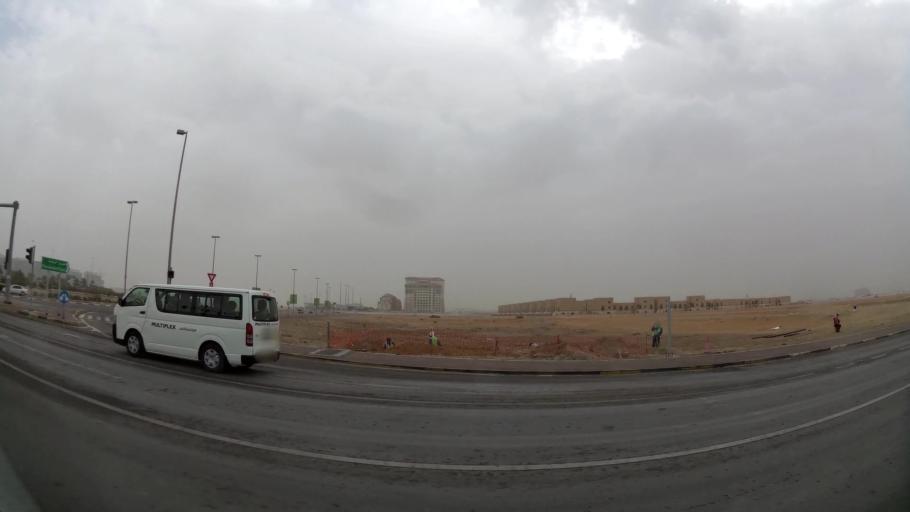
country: AE
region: Abu Dhabi
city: Abu Dhabi
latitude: 24.4406
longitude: 54.6015
